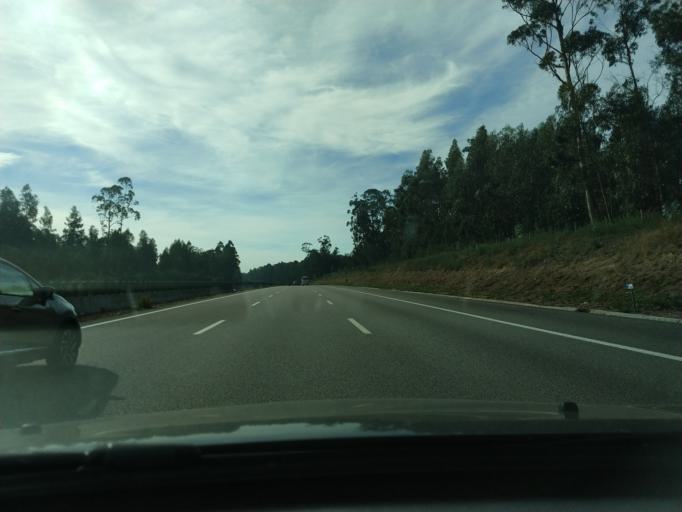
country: PT
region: Aveiro
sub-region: Ovar
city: Valega
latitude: 40.8352
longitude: -8.5549
